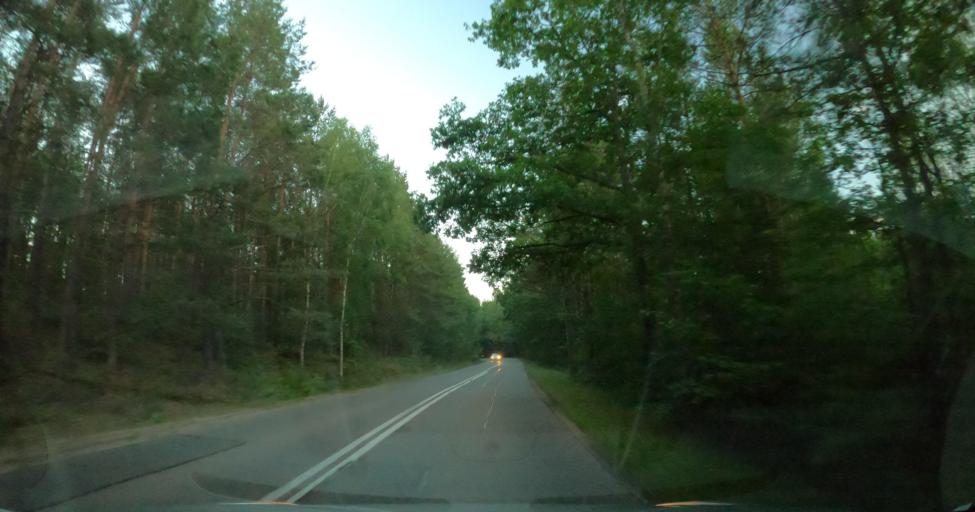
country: PL
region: Pomeranian Voivodeship
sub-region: Powiat wejherowski
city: Linia
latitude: 54.4637
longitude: 17.9960
